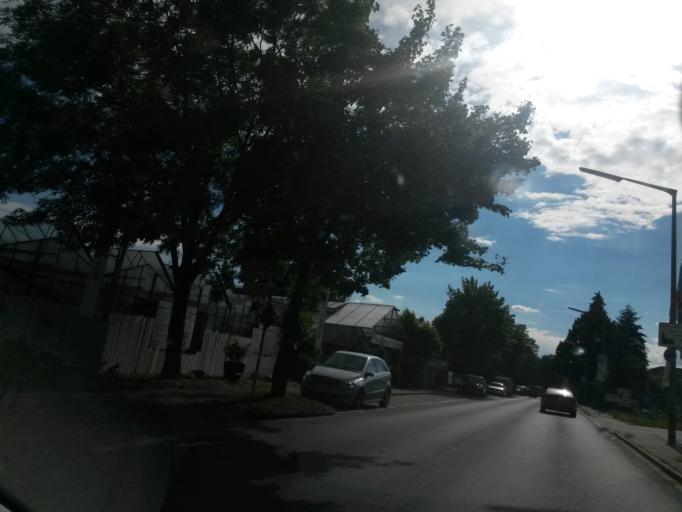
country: DE
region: Bavaria
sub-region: Regierungsbezirk Mittelfranken
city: Zirndorf
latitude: 49.4422
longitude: 10.9704
